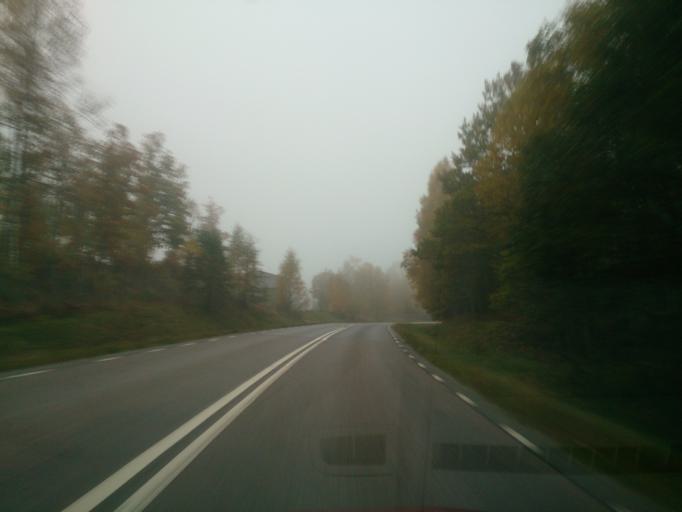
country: SE
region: OEstergoetland
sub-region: Atvidabergs Kommun
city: Atvidaberg
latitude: 58.1628
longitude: 15.9600
